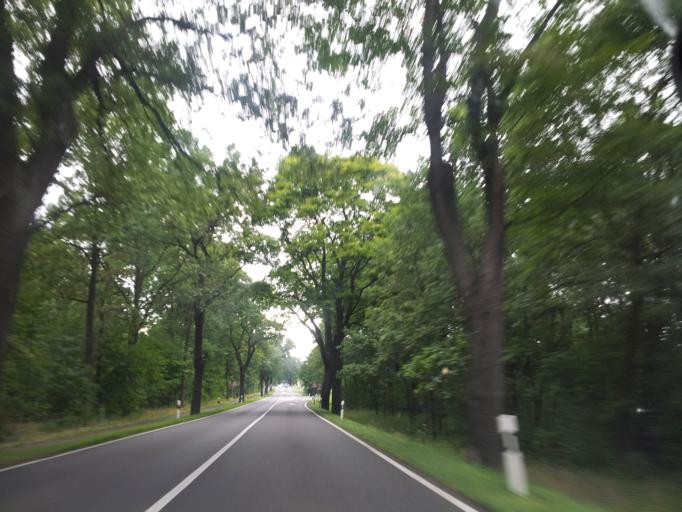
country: DE
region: Brandenburg
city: Treuenbrietzen
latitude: 52.0781
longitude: 12.8832
